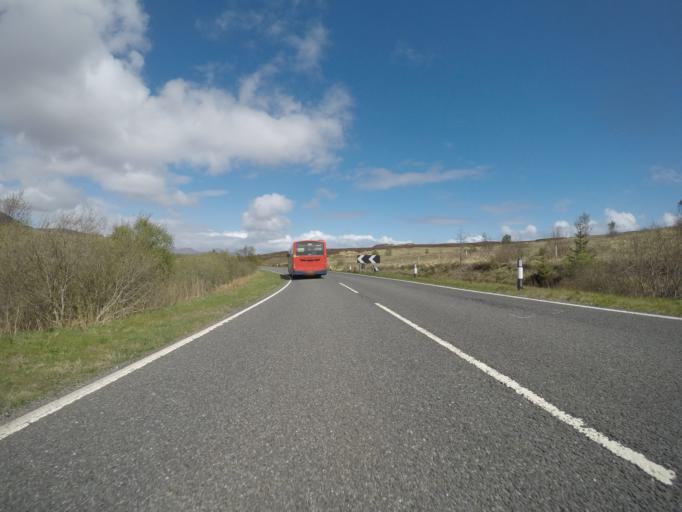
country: GB
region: Scotland
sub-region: Highland
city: Isle of Skye
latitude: 57.3551
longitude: -6.1971
